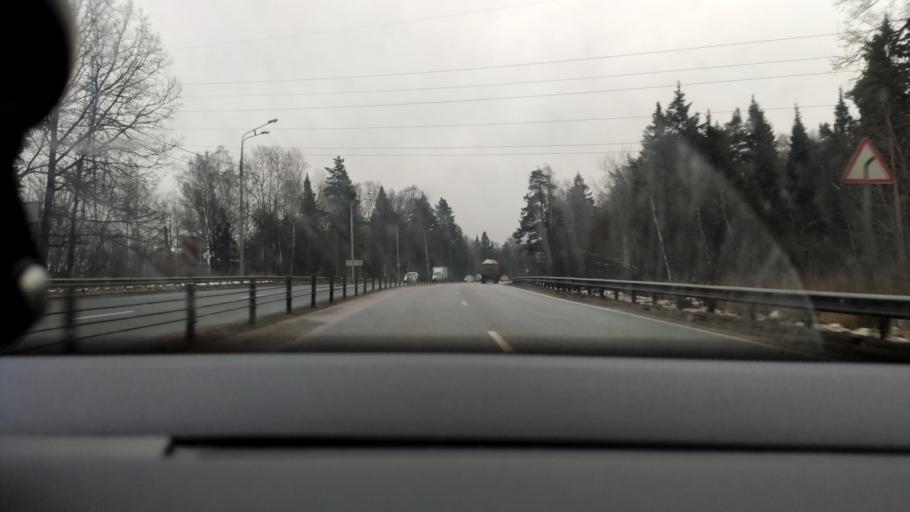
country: RU
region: Moskovskaya
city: Sergiyev Posad
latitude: 56.2626
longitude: 38.1274
